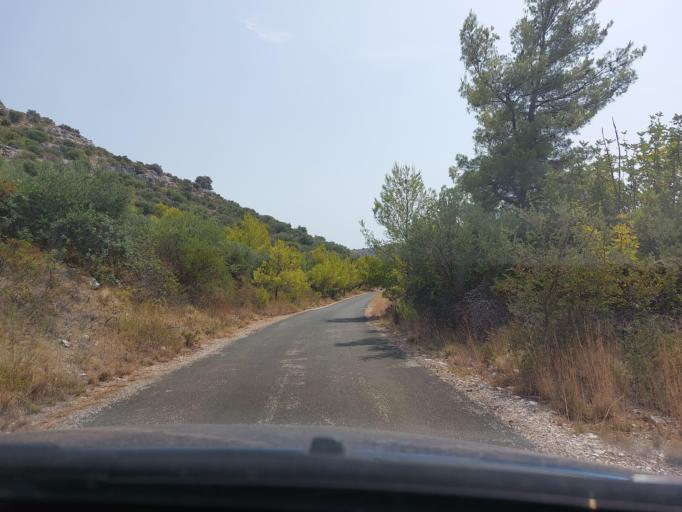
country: HR
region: Dubrovacko-Neretvanska
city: Smokvica
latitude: 42.7374
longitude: 16.8895
